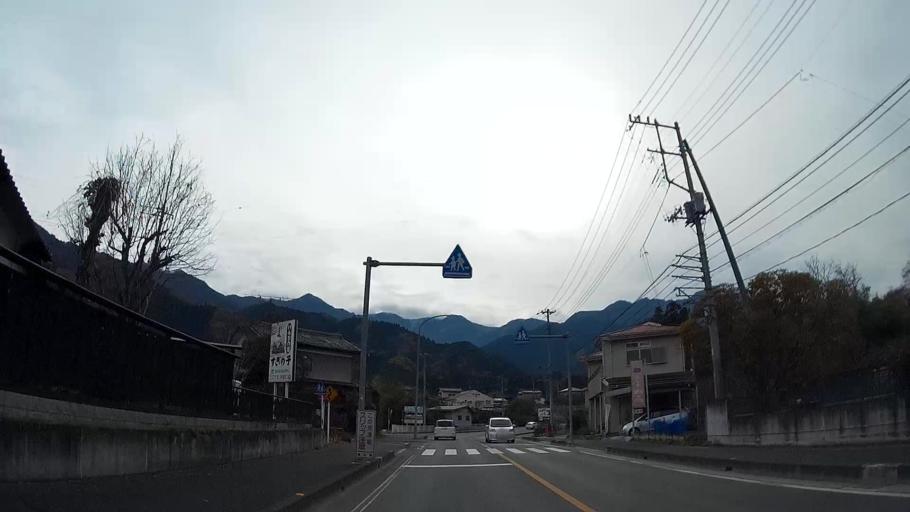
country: JP
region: Saitama
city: Chichibu
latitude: 35.9568
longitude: 139.0302
